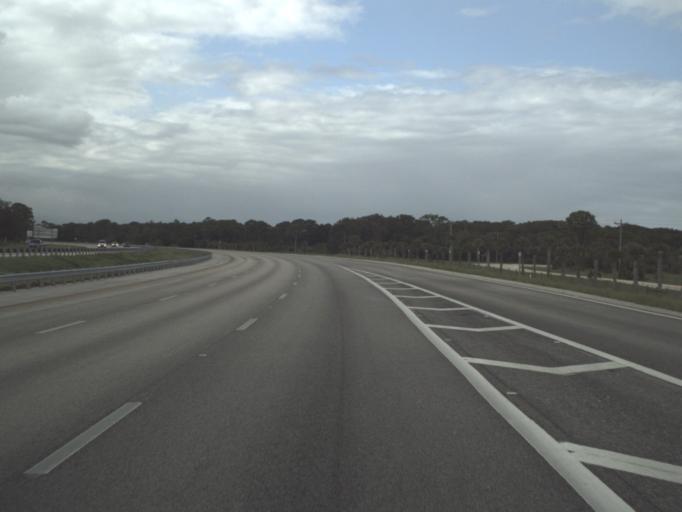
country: US
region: Florida
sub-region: Lee County
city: Tice
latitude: 26.7183
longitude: -81.8141
